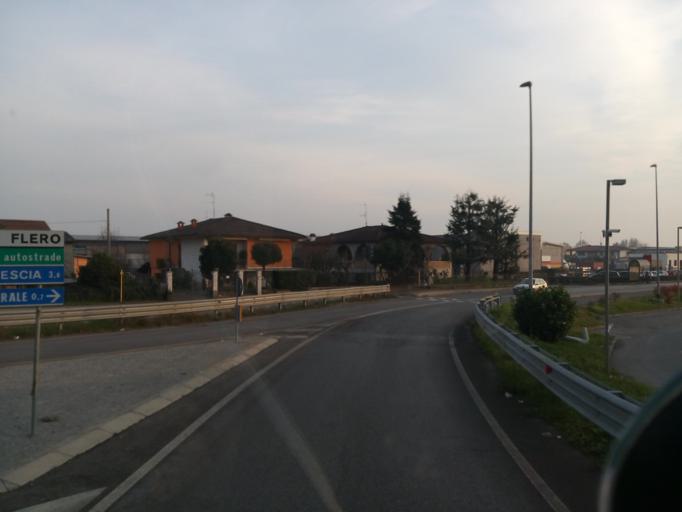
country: IT
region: Lombardy
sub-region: Provincia di Brescia
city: Flero
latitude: 45.4726
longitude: 10.1767
